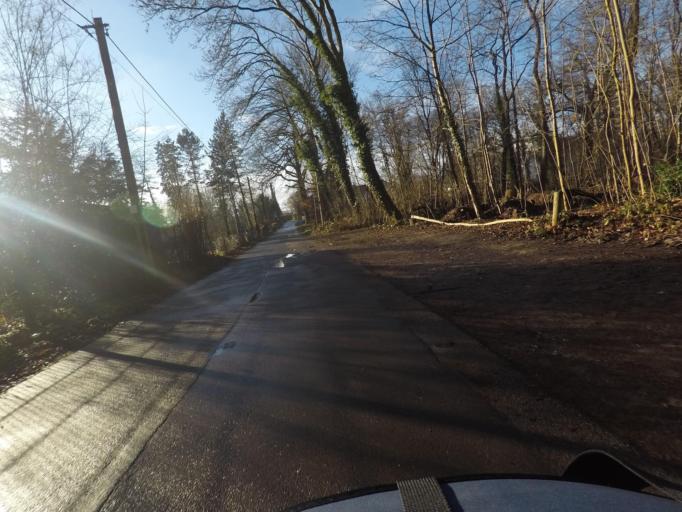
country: DE
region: Baden-Wuerttemberg
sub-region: Karlsruhe Region
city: Ettlingen
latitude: 48.9727
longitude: 8.4148
